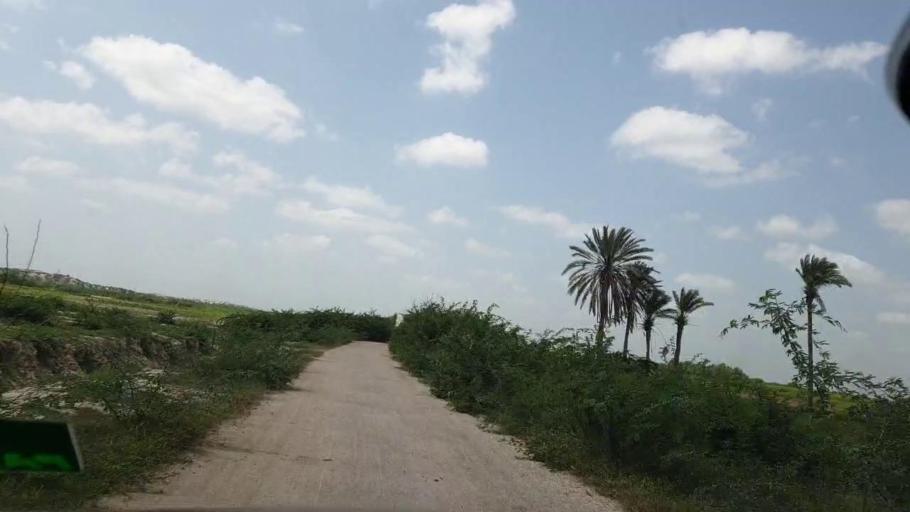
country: PK
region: Sindh
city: Kadhan
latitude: 24.5516
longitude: 69.2057
